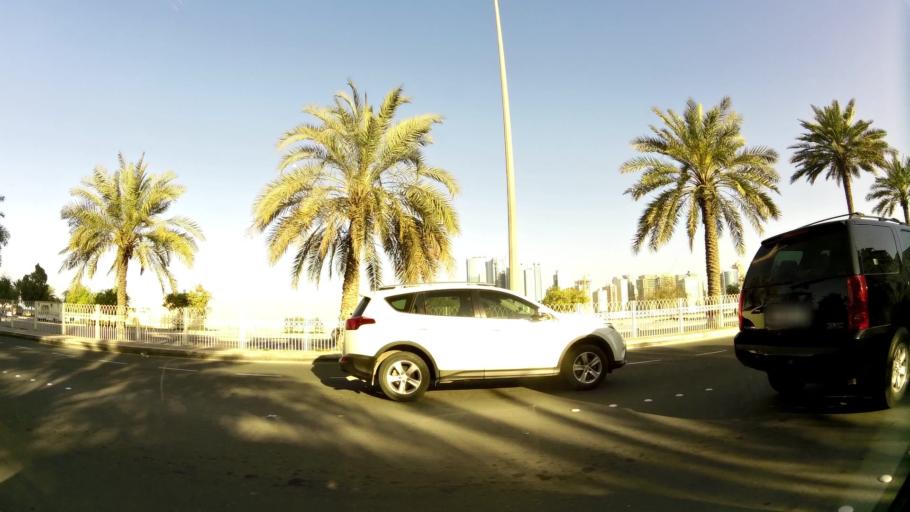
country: BH
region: Manama
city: Manama
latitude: 26.2265
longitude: 50.5984
